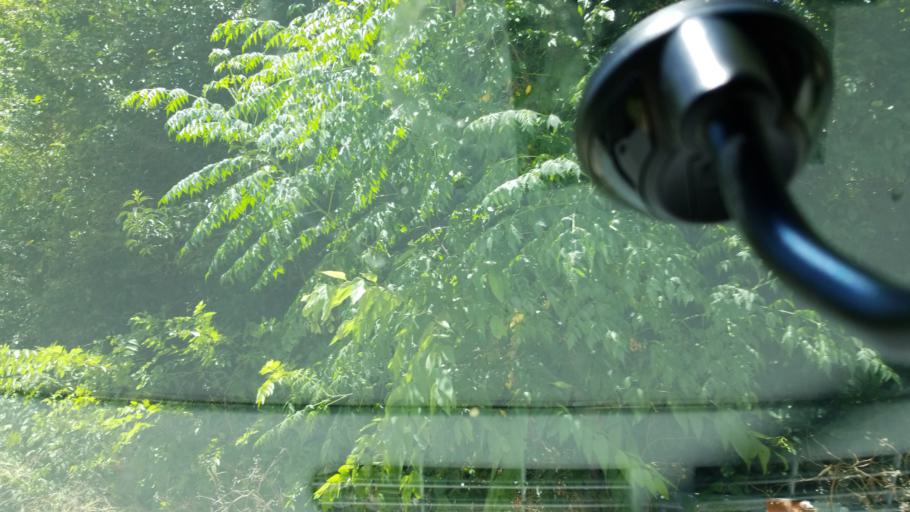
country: US
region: Texas
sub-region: Dallas County
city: Cockrell Hill
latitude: 32.6764
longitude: -96.8210
